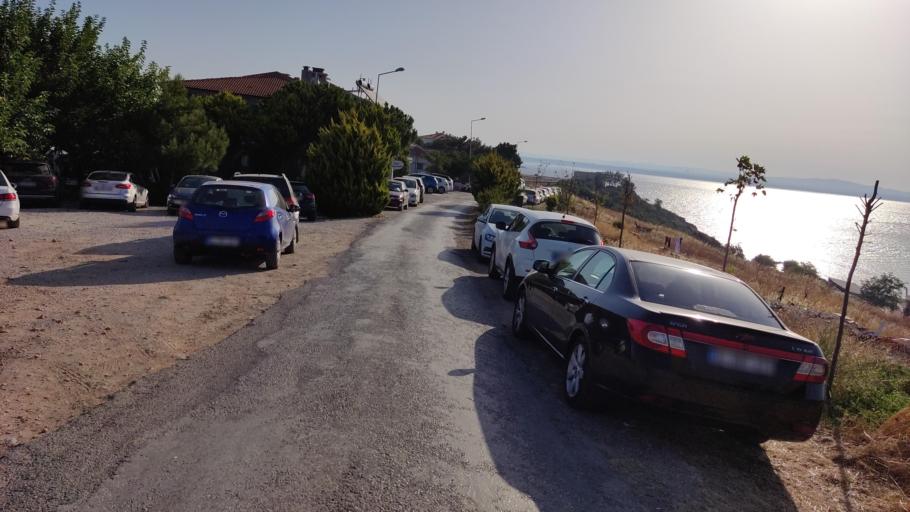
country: TR
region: Canakkale
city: Bozcaada
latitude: 39.8314
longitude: 26.0709
